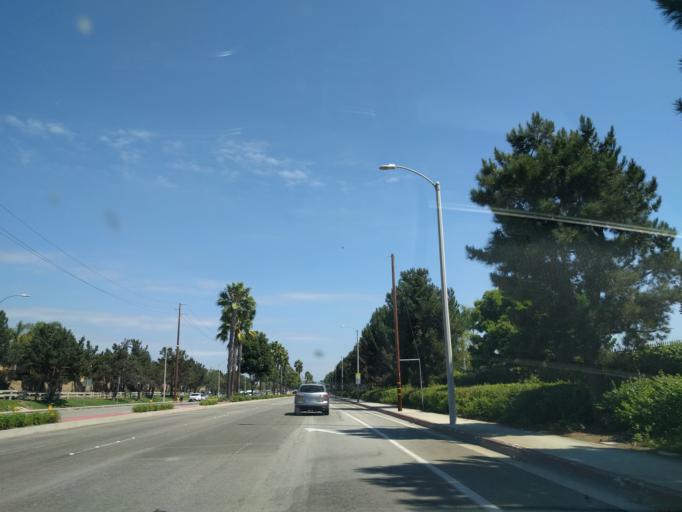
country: US
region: California
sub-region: Orange County
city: Huntington Beach
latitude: 33.6863
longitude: -118.0144
